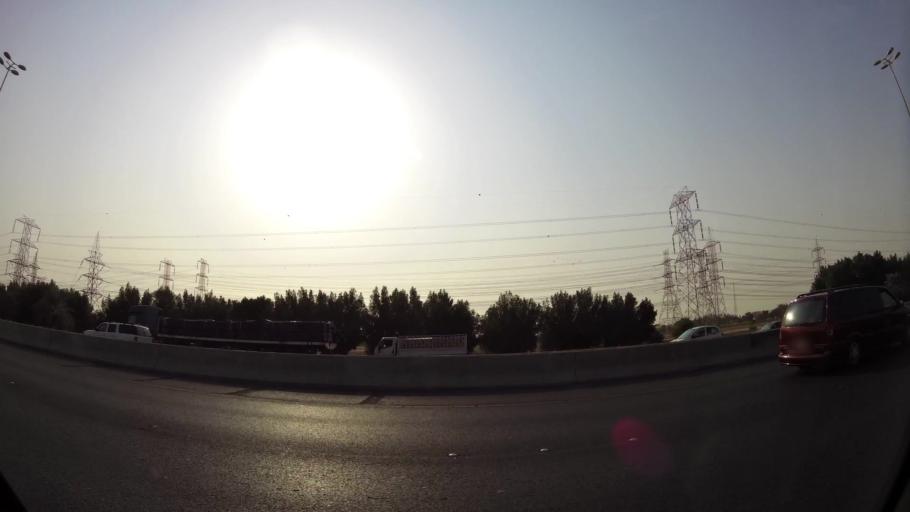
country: KW
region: Mubarak al Kabir
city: Sabah as Salim
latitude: 29.2237
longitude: 48.0548
